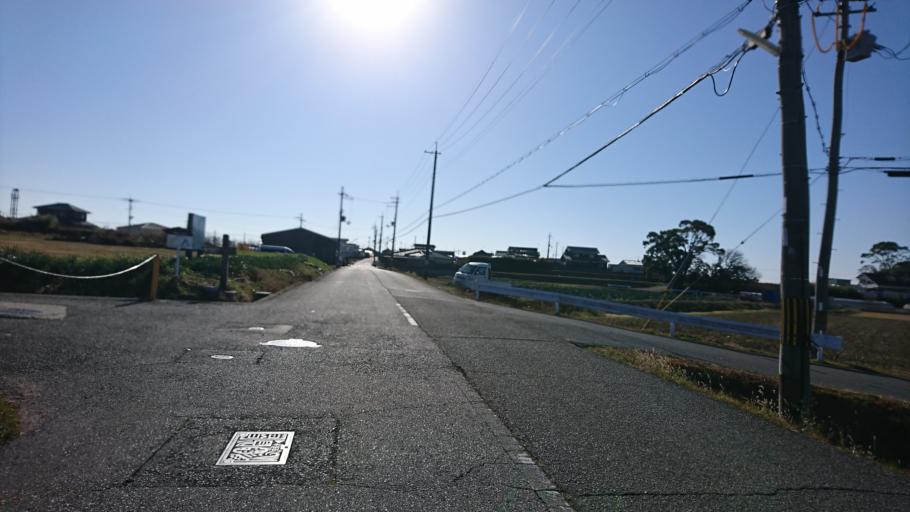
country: JP
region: Hyogo
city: Miki
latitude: 34.7233
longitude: 134.9587
